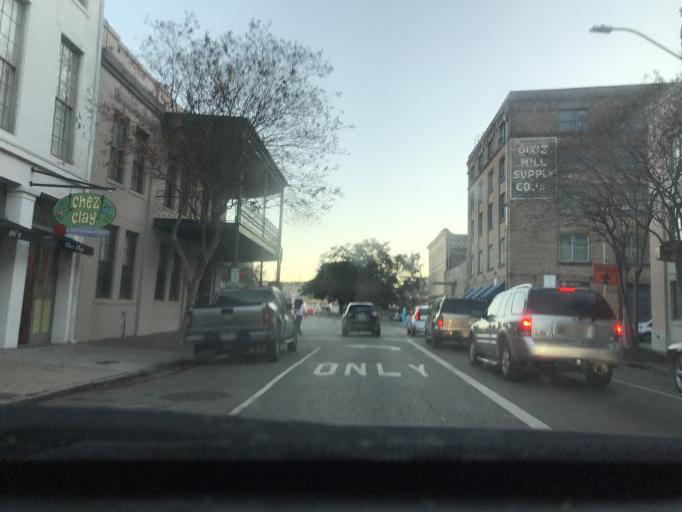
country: US
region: Louisiana
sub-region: Orleans Parish
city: New Orleans
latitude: 29.9437
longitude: -90.0675
